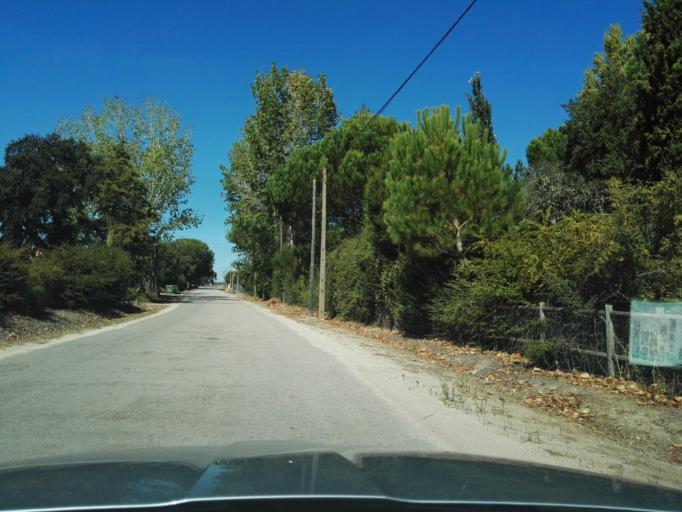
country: PT
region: Santarem
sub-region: Benavente
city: Poceirao
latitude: 38.8609
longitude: -8.7349
